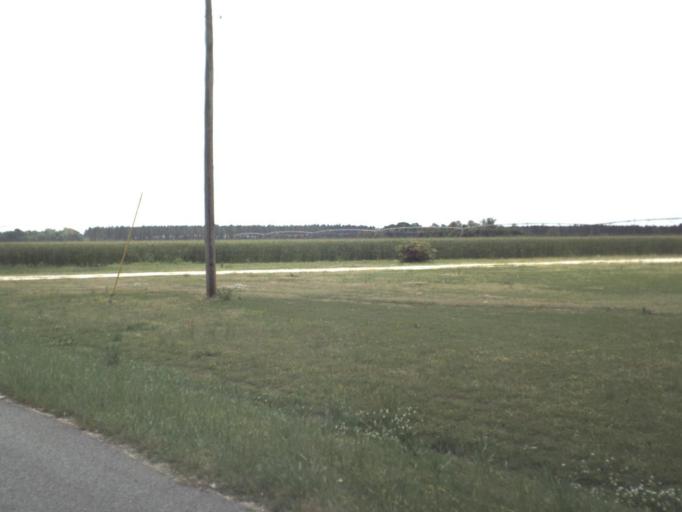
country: US
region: Alabama
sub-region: Escambia County
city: Atmore
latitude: 30.9786
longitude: -87.4906
